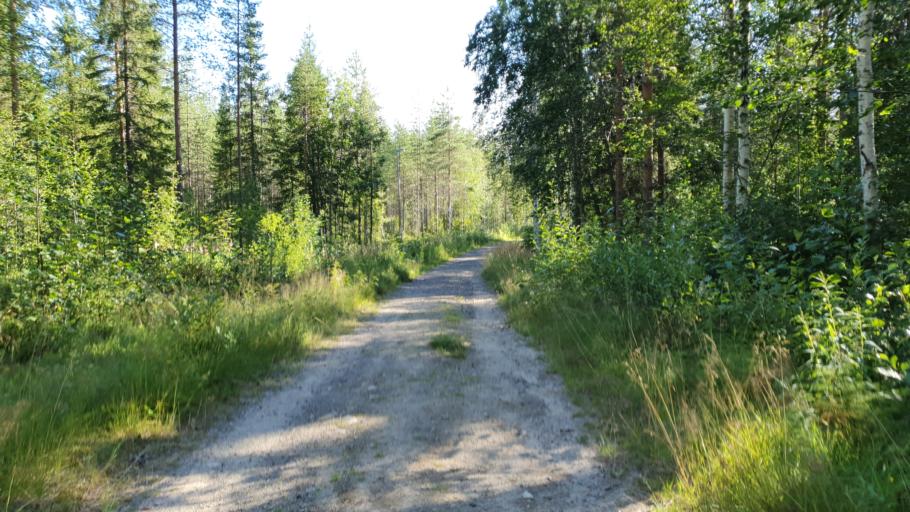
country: FI
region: Kainuu
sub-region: Kehys-Kainuu
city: Kuhmo
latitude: 64.1119
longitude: 29.5052
